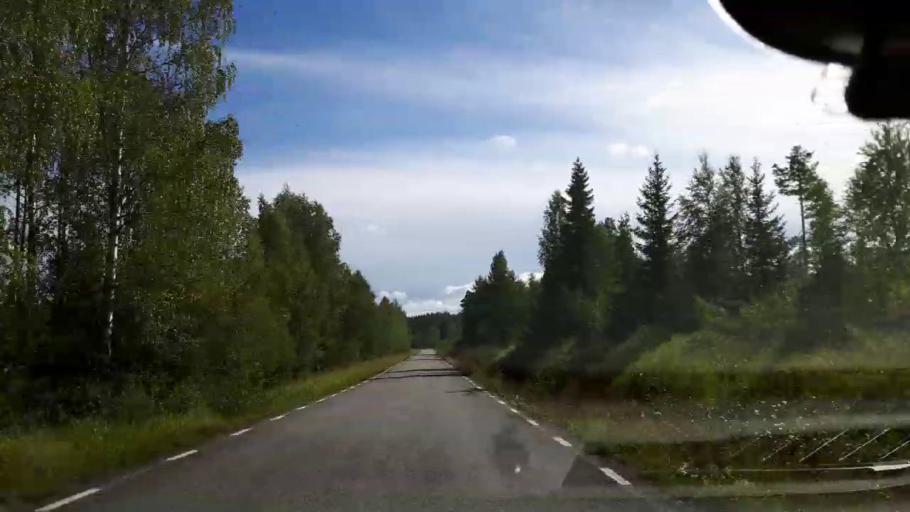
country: SE
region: Jaemtland
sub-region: OEstersunds Kommun
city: Lit
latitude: 63.2288
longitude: 15.2692
